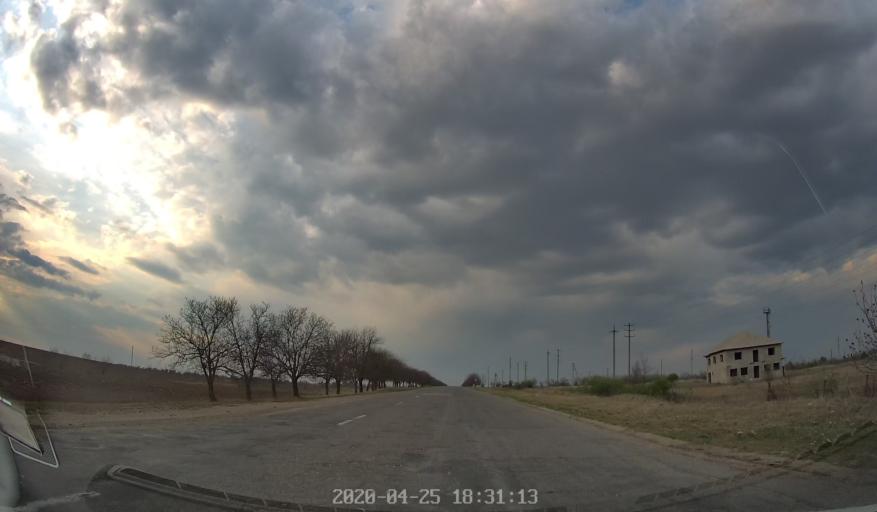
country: MD
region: Criuleni
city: Criuleni
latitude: 47.2148
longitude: 29.1480
